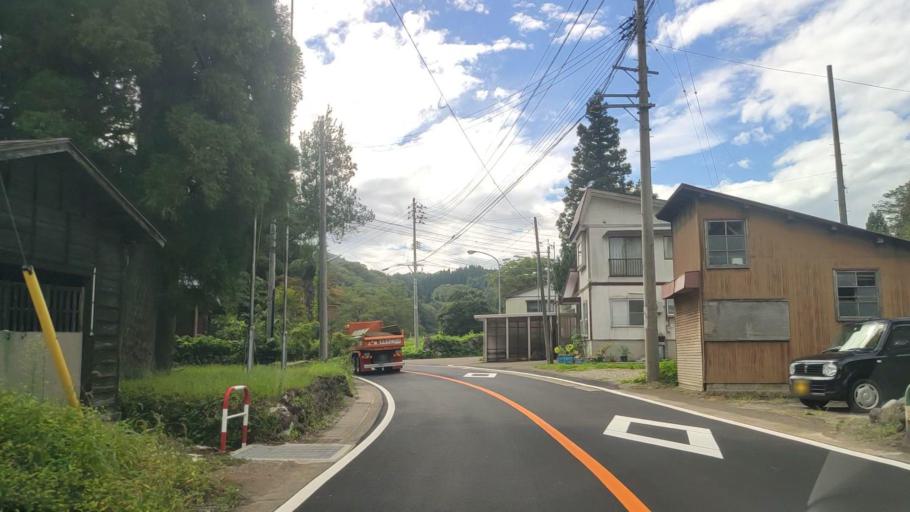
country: JP
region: Niigata
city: Arai
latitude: 36.9580
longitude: 138.2704
